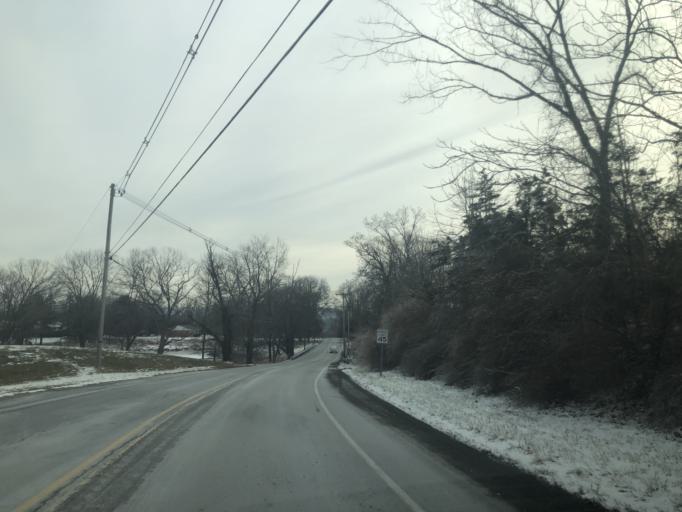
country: US
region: New Jersey
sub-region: Warren County
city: Belvidere
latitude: 40.9336
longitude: -75.0121
